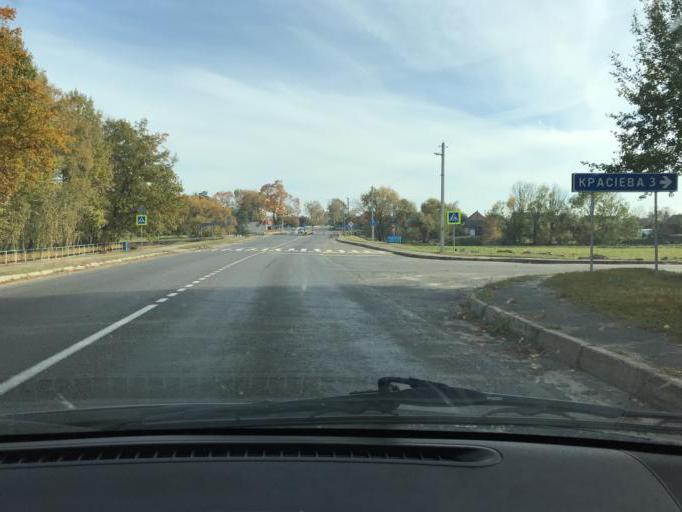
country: BY
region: Brest
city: Asnyezhytsy
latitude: 52.1982
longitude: 26.0667
